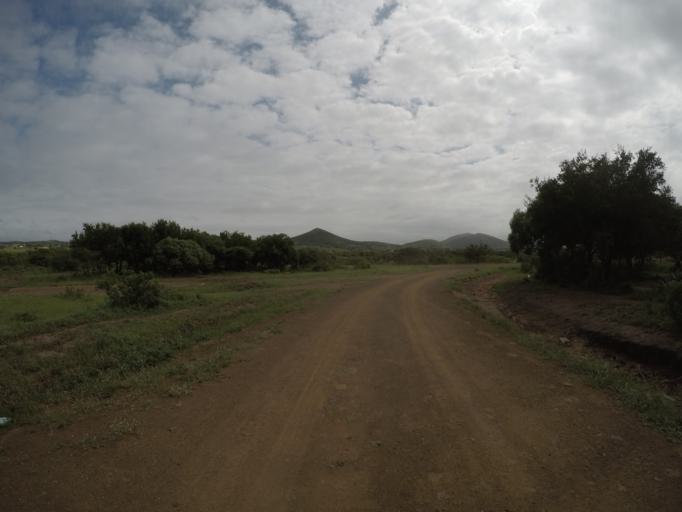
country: ZA
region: KwaZulu-Natal
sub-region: uThungulu District Municipality
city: Empangeni
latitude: -28.6209
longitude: 31.8559
